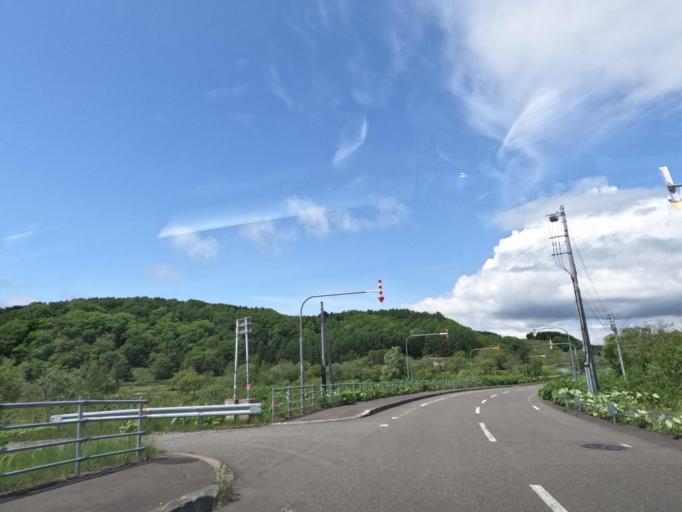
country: JP
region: Hokkaido
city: Tobetsu
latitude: 43.3903
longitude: 141.5792
